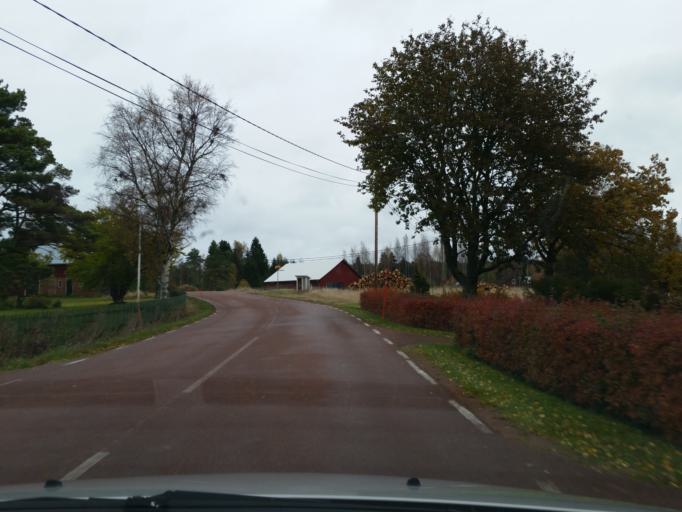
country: AX
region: Alands landsbygd
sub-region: Lemland
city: Lemland
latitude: 60.0596
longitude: 20.0966
